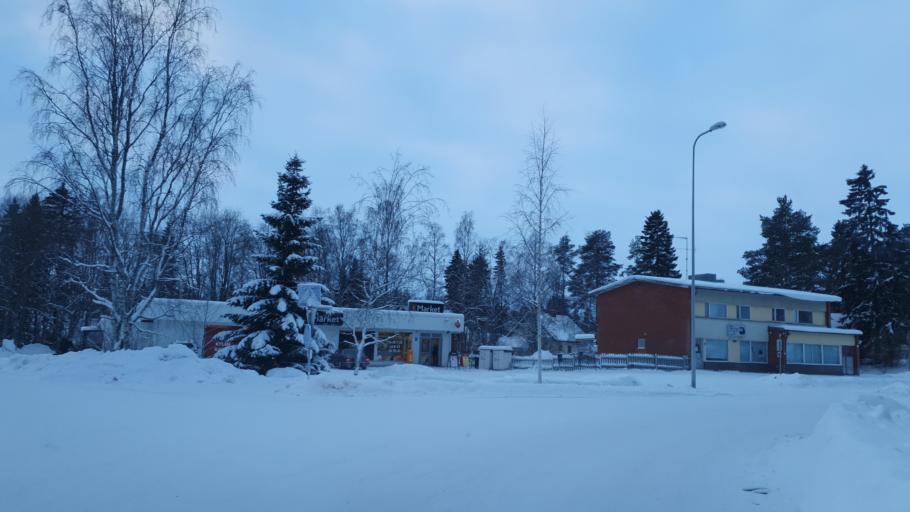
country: FI
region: Northern Ostrobothnia
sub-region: Oulu
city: Haukipudas
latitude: 65.2126
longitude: 25.3100
